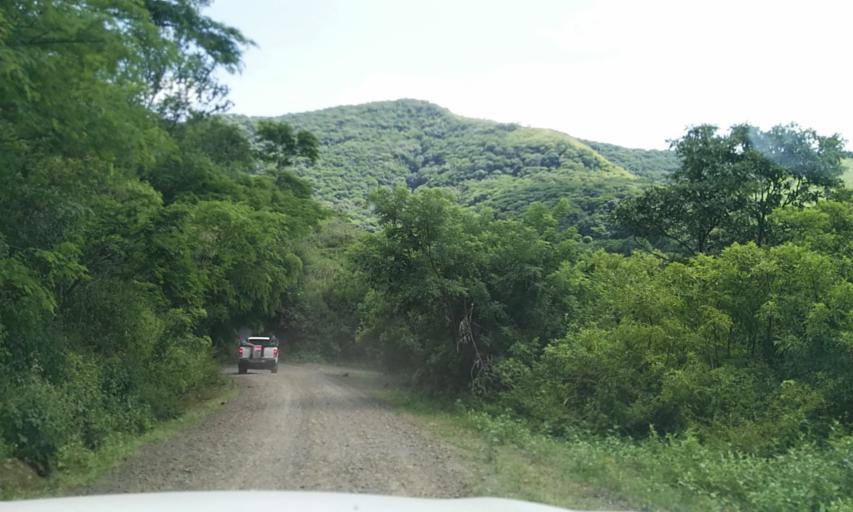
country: NI
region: Matagalpa
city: Terrabona
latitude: 12.6990
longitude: -85.9372
